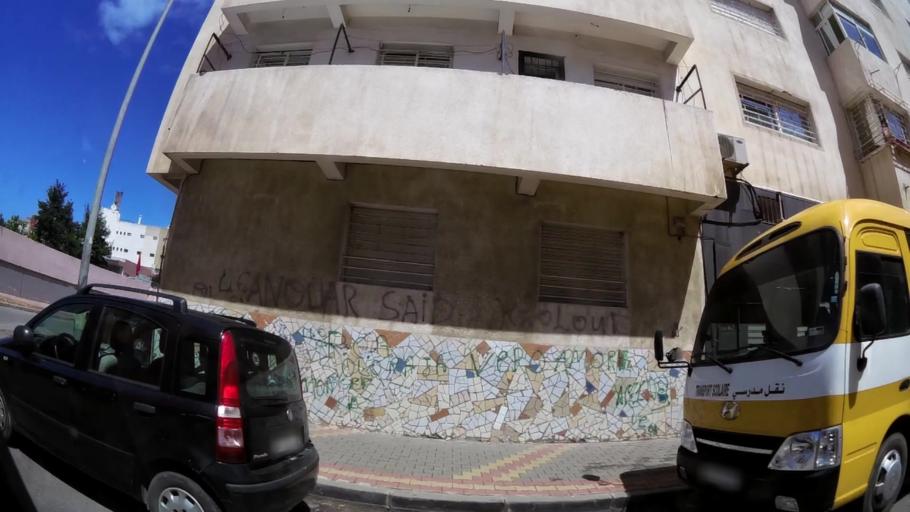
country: MA
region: Grand Casablanca
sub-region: Mediouna
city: Tit Mellil
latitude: 33.6035
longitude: -7.5261
